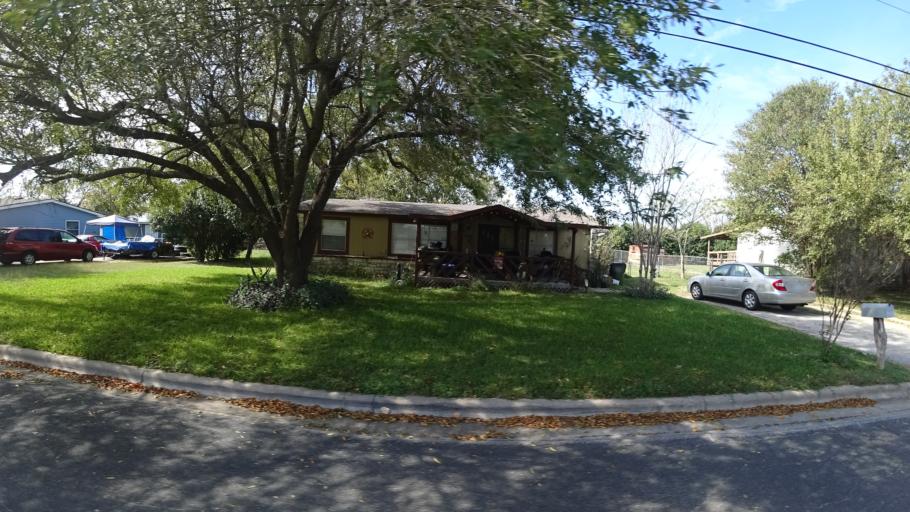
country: US
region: Texas
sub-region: Travis County
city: Pflugerville
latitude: 30.4114
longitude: -97.6336
